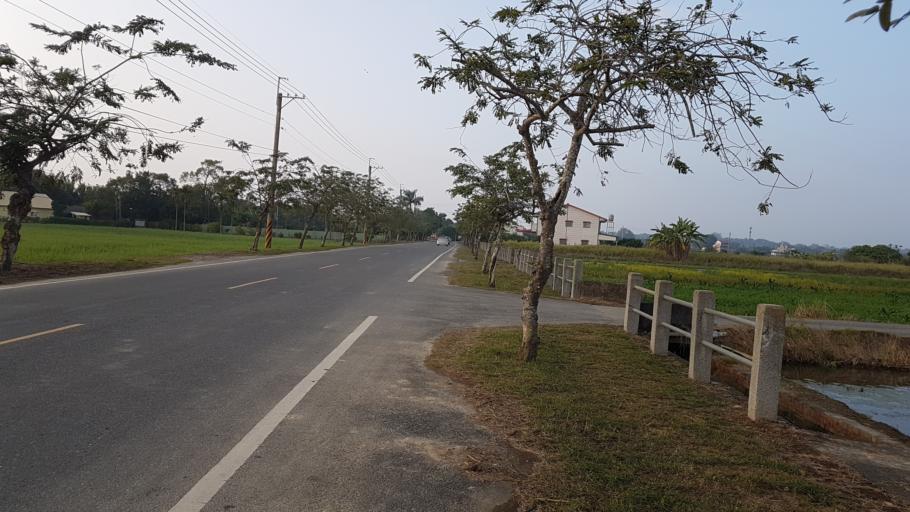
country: TW
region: Taiwan
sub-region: Chiayi
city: Jiayi Shi
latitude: 23.3710
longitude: 120.4501
